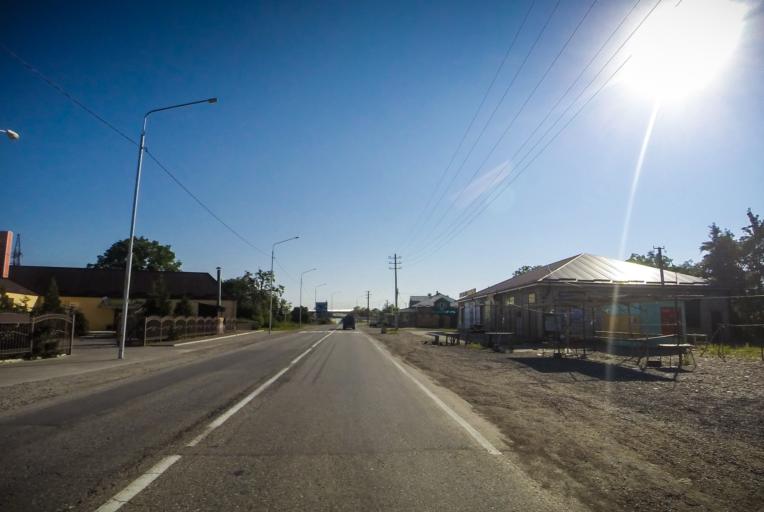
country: RU
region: North Ossetia
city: Arkhonskaya
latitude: 43.1163
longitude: 44.4969
